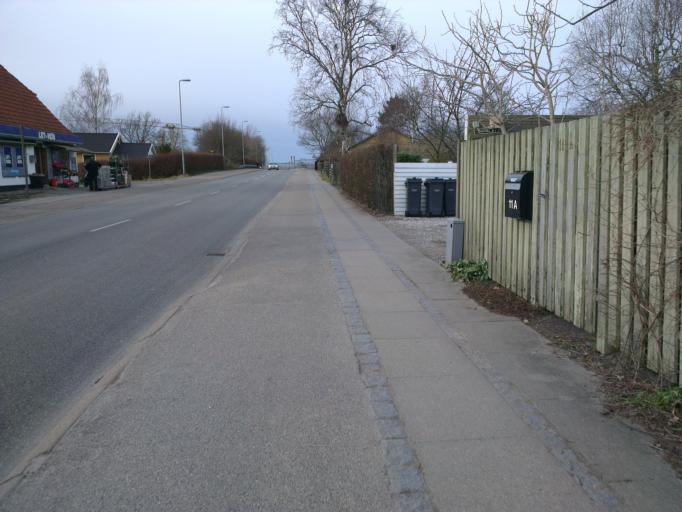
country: DK
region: Capital Region
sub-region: Frederikssund Kommune
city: Frederikssund
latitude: 55.8280
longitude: 12.0716
